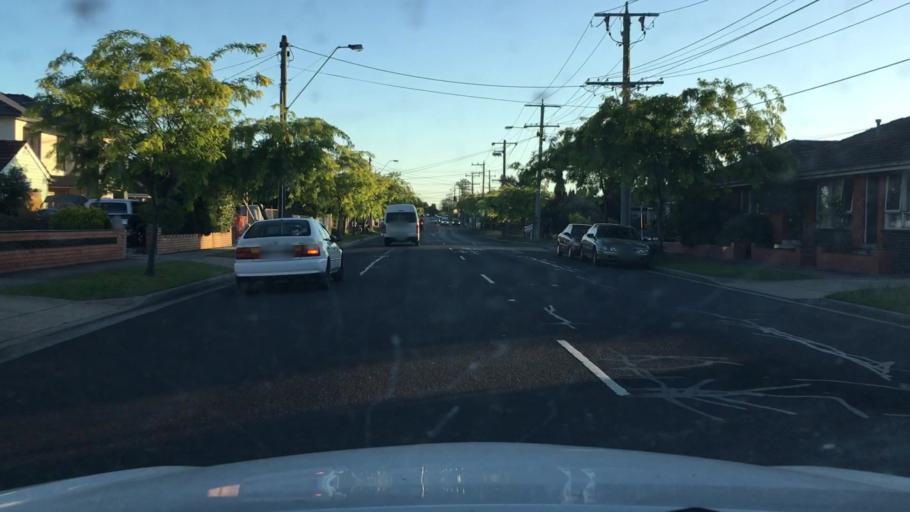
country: AU
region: Victoria
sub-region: Greater Dandenong
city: Noble Park
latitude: -37.9628
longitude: 145.1689
